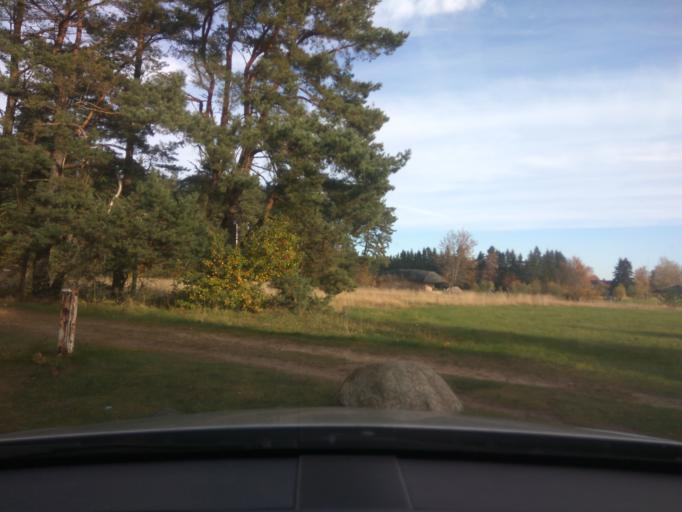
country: LV
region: Alsunga
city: Alsunga
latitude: 57.0055
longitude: 21.3815
